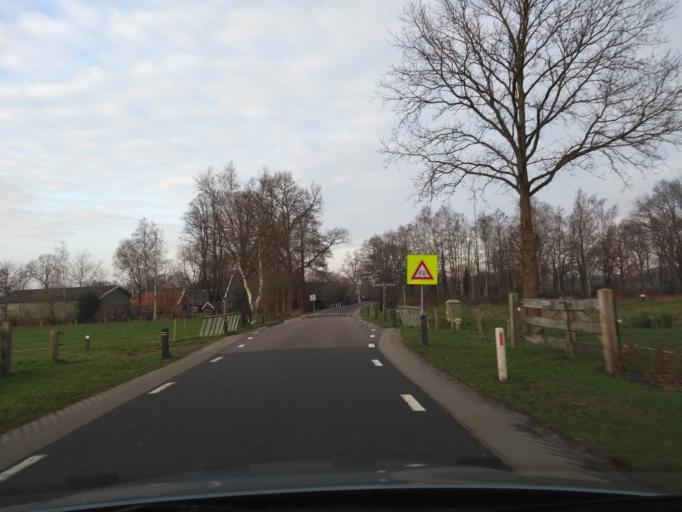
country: NL
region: Overijssel
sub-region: Gemeente Almelo
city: Almelo
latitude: 52.3181
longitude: 6.6947
